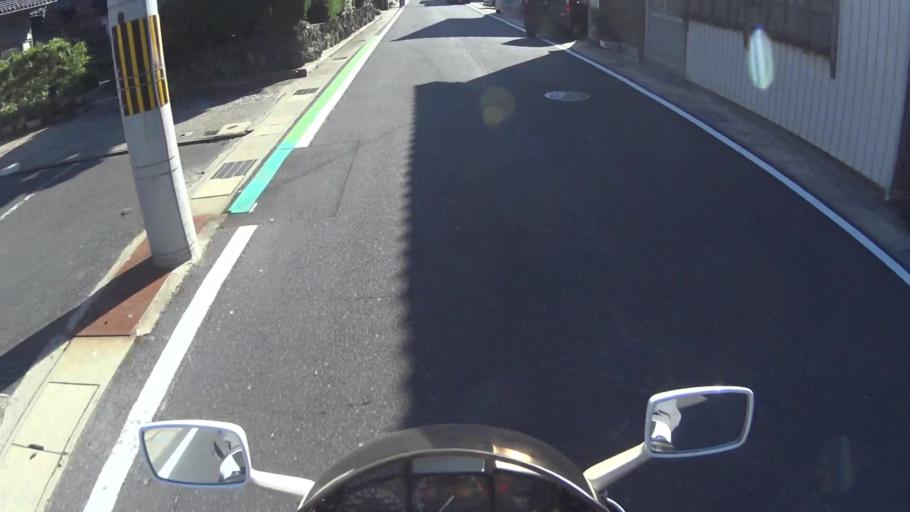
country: JP
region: Kyoto
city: Miyazu
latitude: 35.7397
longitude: 135.0949
